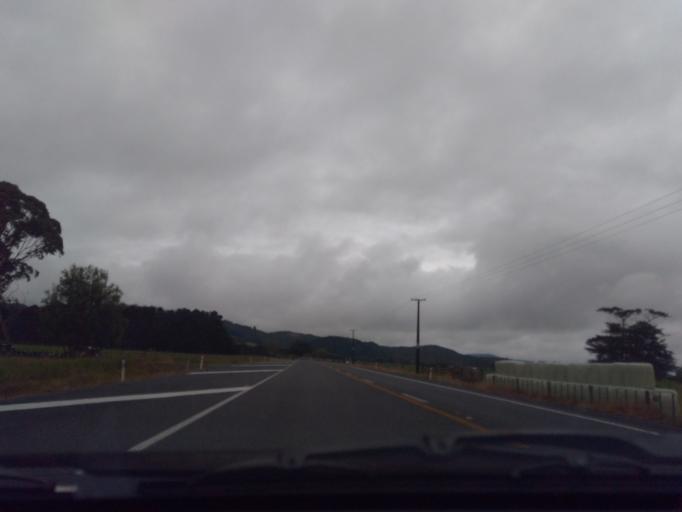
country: NZ
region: Northland
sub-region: Whangarei
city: Ruakaka
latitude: -36.0078
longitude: 174.4166
